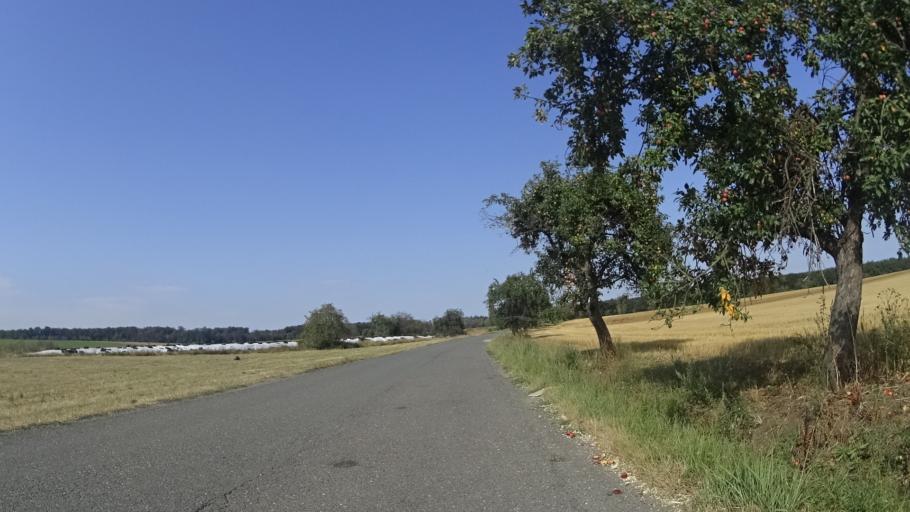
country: CZ
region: Kralovehradecky
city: Novy Bydzov
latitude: 50.2785
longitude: 15.5478
